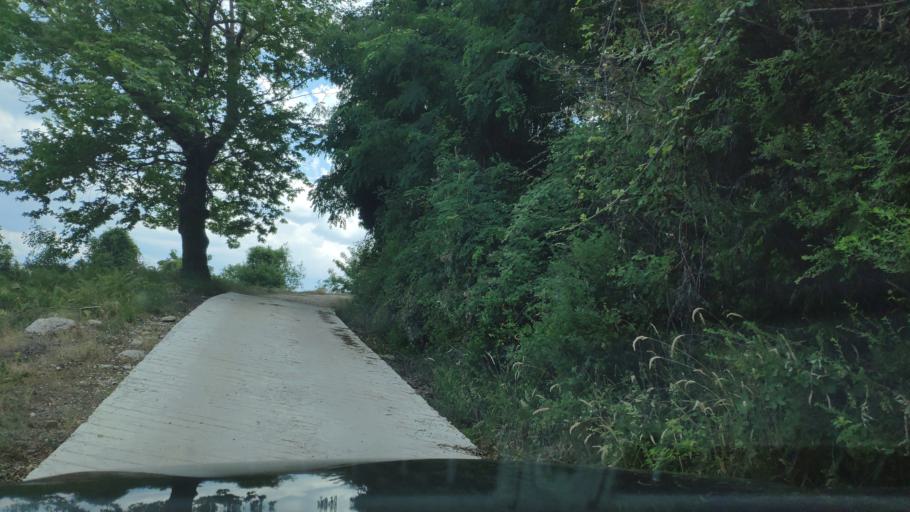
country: GR
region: Epirus
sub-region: Nomos Artas
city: Agios Dimitrios
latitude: 39.3193
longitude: 21.0006
